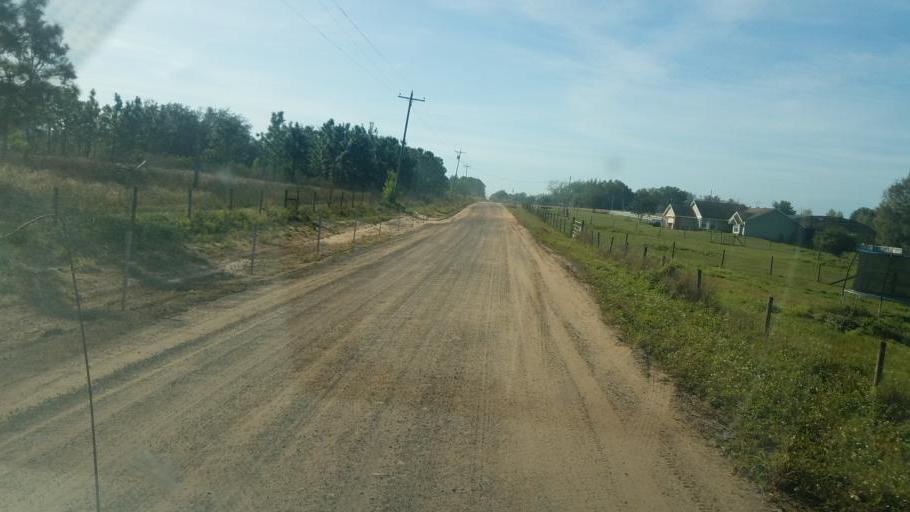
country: US
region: Florida
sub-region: Lake County
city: Clermont
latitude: 28.4556
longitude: -81.7570
